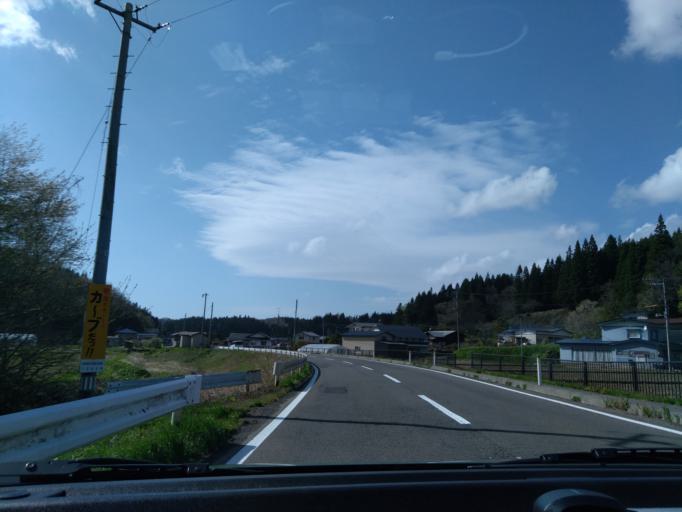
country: JP
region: Akita
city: Akita
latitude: 39.7111
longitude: 140.2037
